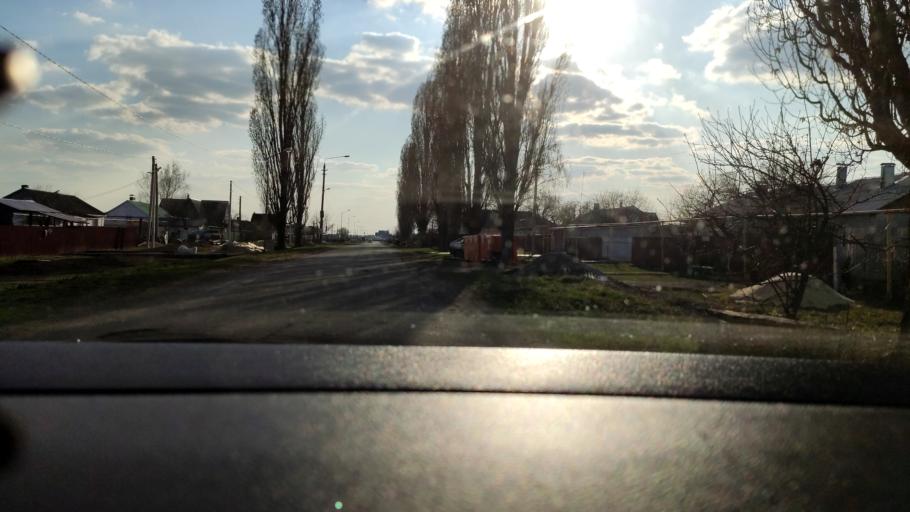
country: RU
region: Voronezj
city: Maslovka
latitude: 51.5034
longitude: 39.3028
